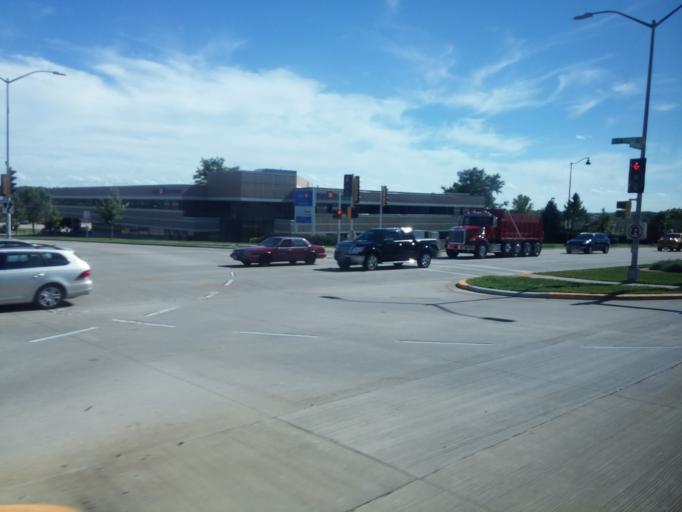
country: US
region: Wisconsin
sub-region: Dane County
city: Monona
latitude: 43.1318
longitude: -89.3030
